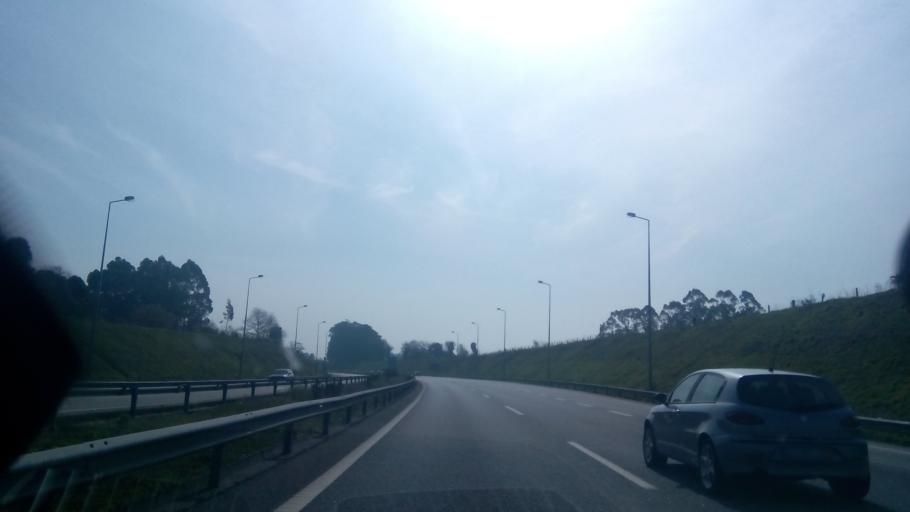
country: PT
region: Porto
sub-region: Vila do Conde
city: Arvore
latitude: 41.3244
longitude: -8.7081
